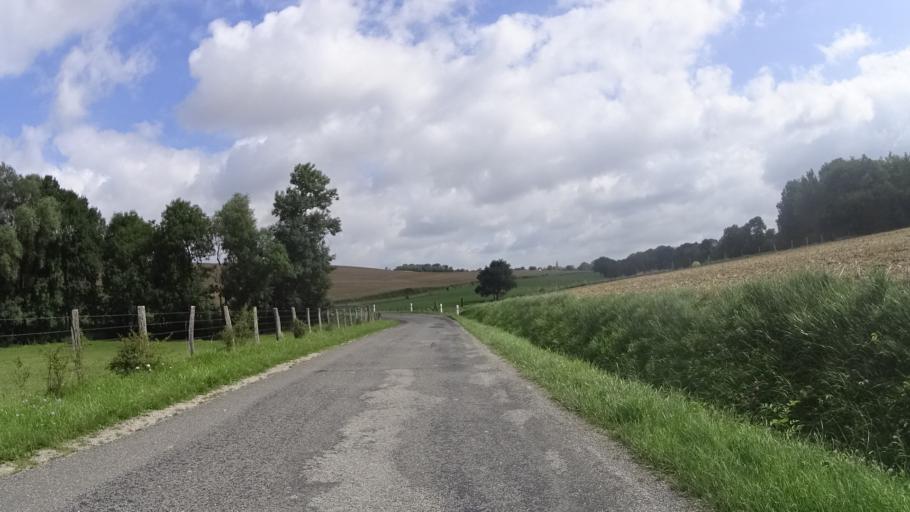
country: FR
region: Lorraine
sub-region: Departement de la Meuse
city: Ligny-en-Barrois
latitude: 48.7326
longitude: 5.3784
